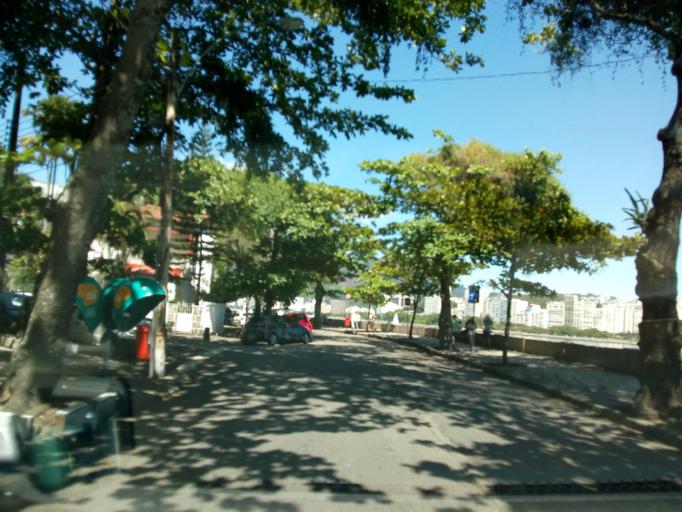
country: BR
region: Rio de Janeiro
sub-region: Rio De Janeiro
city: Rio de Janeiro
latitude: -22.9434
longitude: -43.1612
